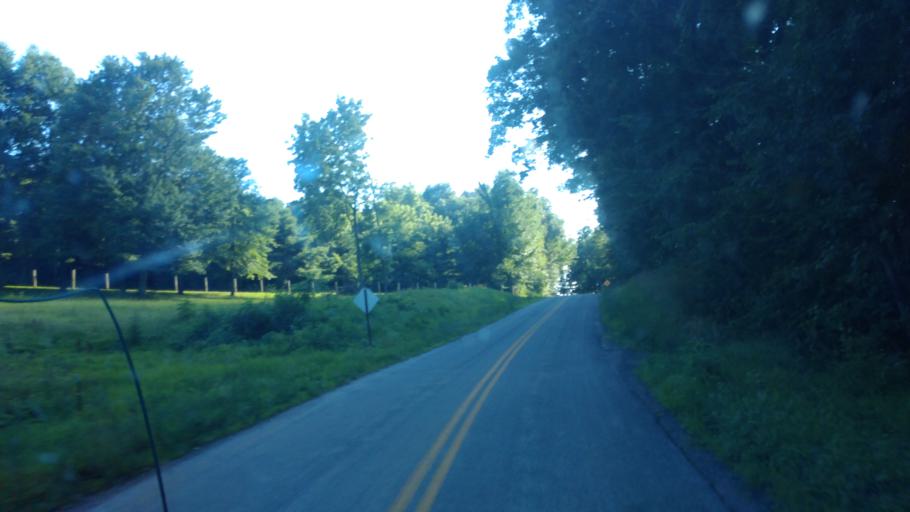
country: US
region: Ohio
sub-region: Ashland County
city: Loudonville
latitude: 40.7024
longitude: -82.2005
